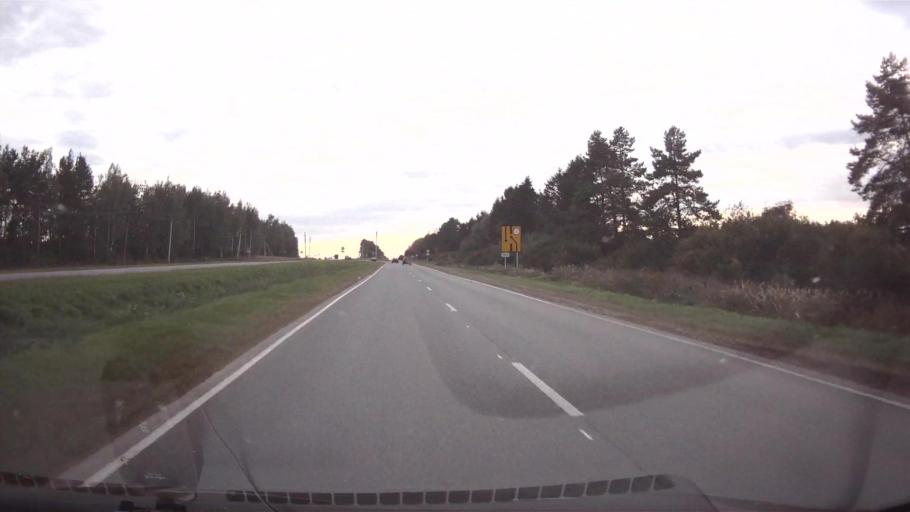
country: RU
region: Mariy-El
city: Yoshkar-Ola
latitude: 56.7214
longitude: 48.1069
